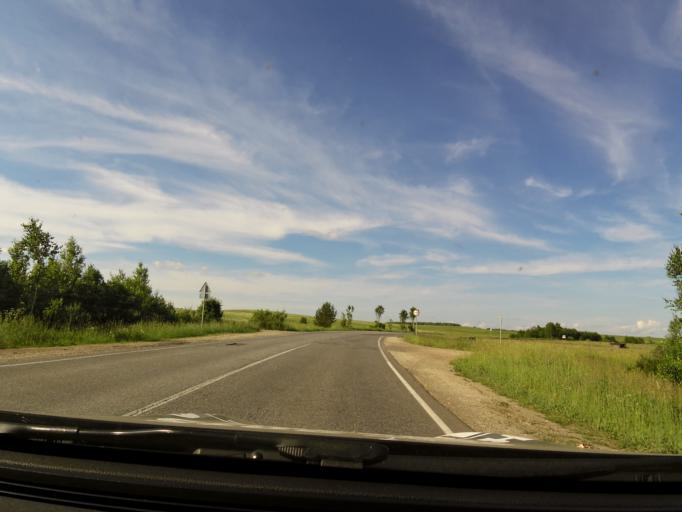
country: RU
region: Kirov
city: Belaya Kholunitsa
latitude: 58.8903
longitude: 50.8758
